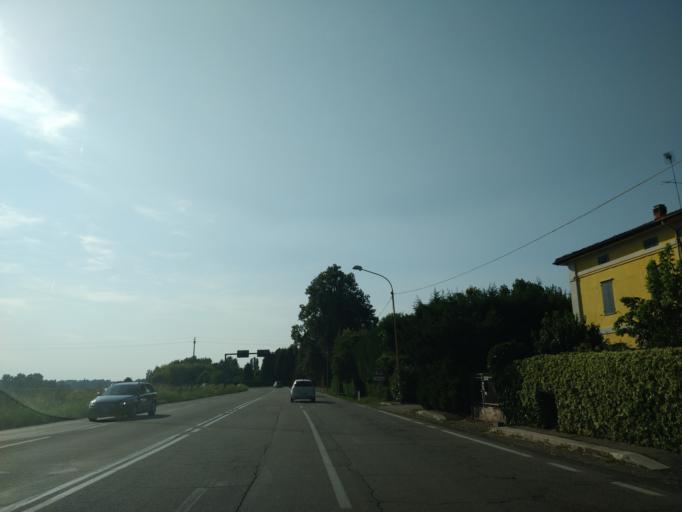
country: IT
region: Emilia-Romagna
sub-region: Provincia di Bologna
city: Argelato
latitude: 44.6559
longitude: 11.3244
